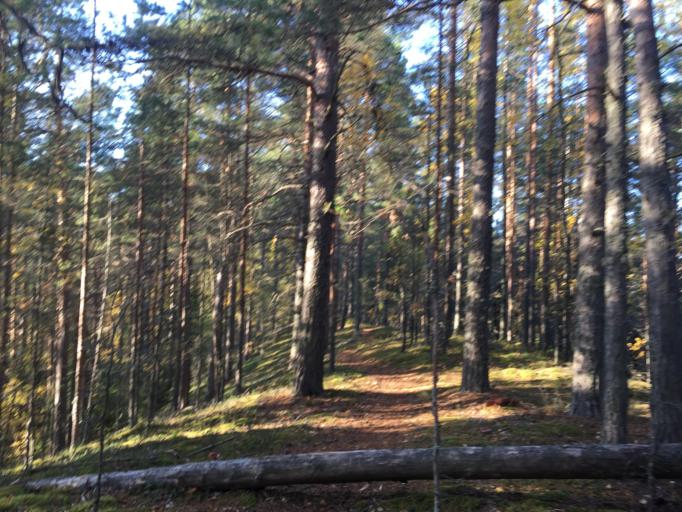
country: RU
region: Leningrad
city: Priozersk
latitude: 61.2807
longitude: 30.1236
